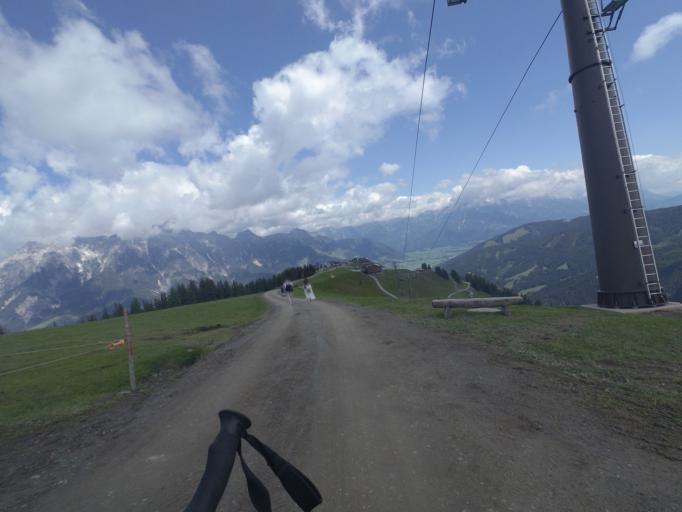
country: AT
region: Salzburg
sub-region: Politischer Bezirk Zell am See
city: Viehhofen
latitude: 47.4068
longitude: 12.7092
